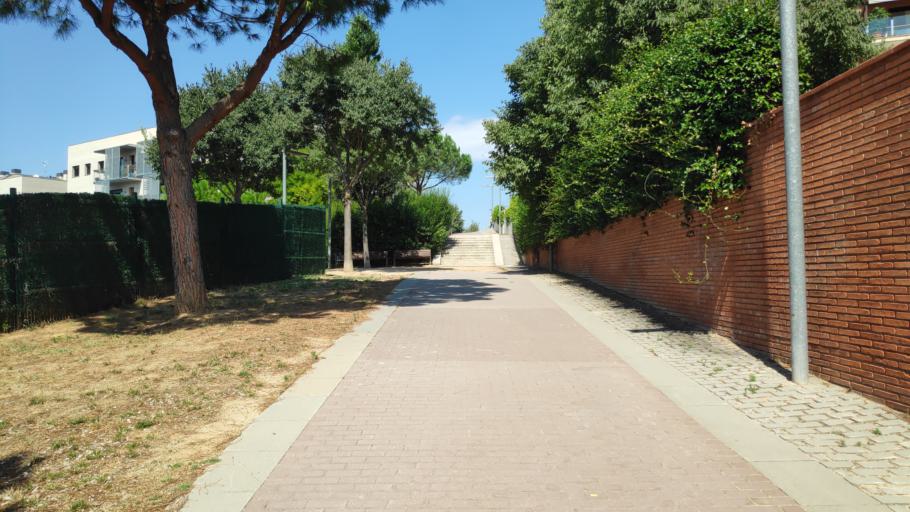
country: ES
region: Catalonia
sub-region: Provincia de Barcelona
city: Sant Cugat del Valles
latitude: 41.4715
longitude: 2.0588
